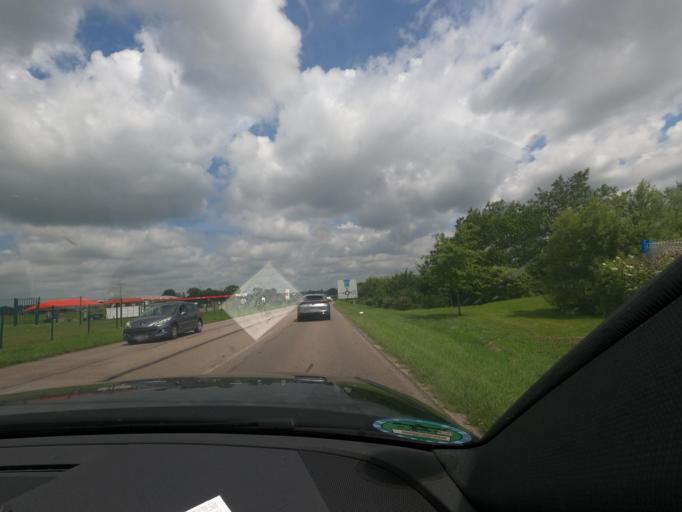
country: FR
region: Haute-Normandie
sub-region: Departement de la Seine-Maritime
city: Sainte-Marie-des-Champs
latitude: 49.6249
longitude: 0.7857
